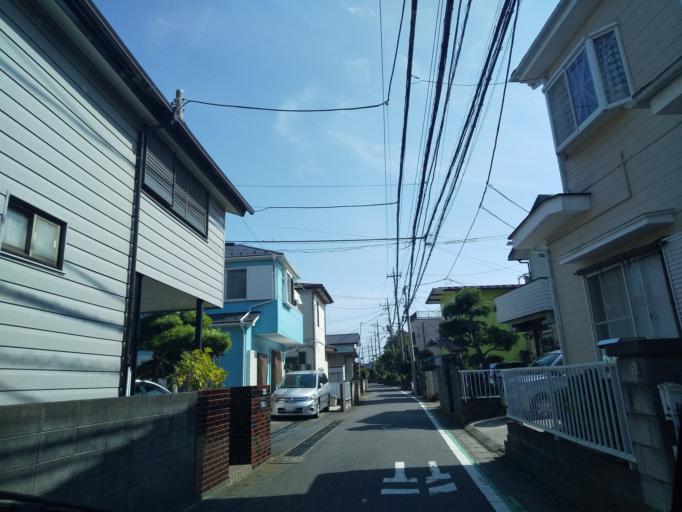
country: JP
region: Kanagawa
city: Minami-rinkan
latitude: 35.4639
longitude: 139.4181
